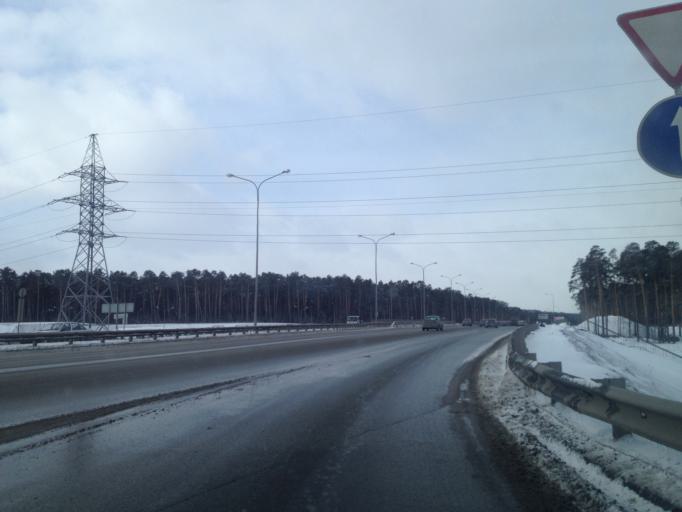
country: RU
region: Sverdlovsk
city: Sovkhoznyy
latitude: 56.7906
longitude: 60.5996
